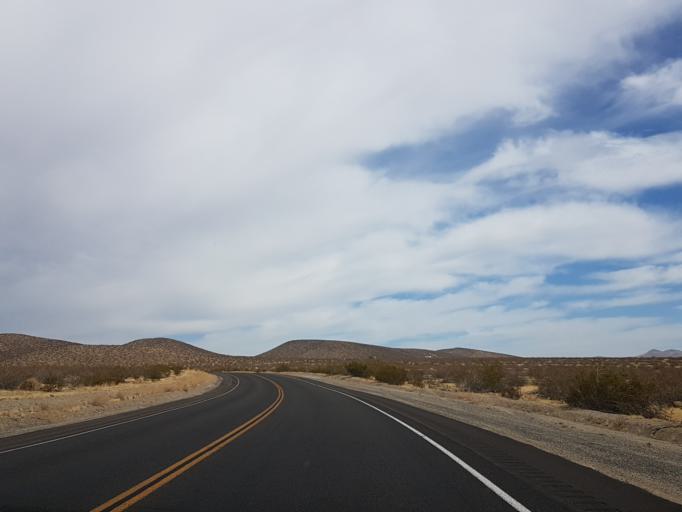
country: US
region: California
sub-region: Kern County
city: Ridgecrest
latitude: 35.4280
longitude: -117.6815
